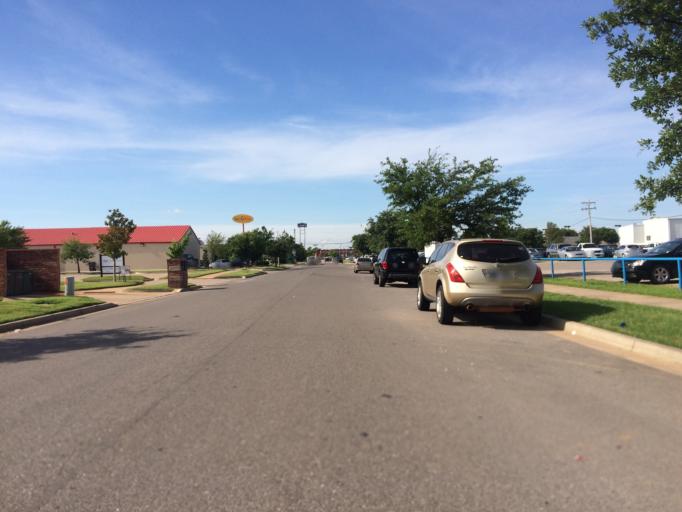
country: US
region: Oklahoma
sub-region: Cleveland County
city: Norman
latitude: 35.2273
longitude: -97.4828
